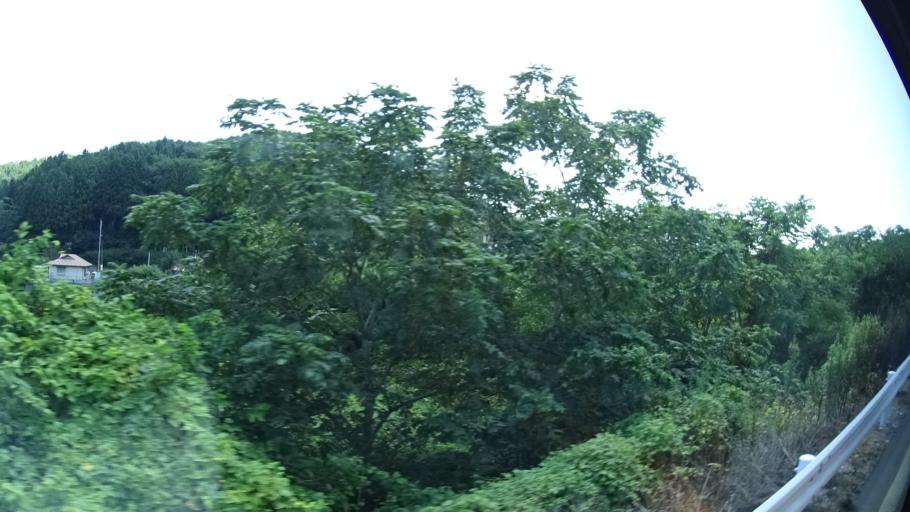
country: JP
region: Iwate
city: Ofunato
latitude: 39.0074
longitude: 141.7141
